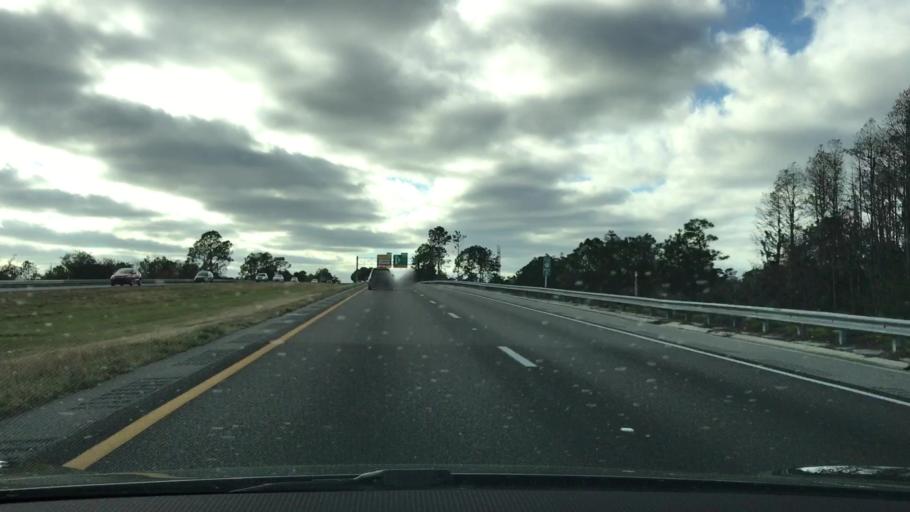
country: US
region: Florida
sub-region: Orange County
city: Hunters Creek
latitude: 28.3581
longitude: -81.4485
